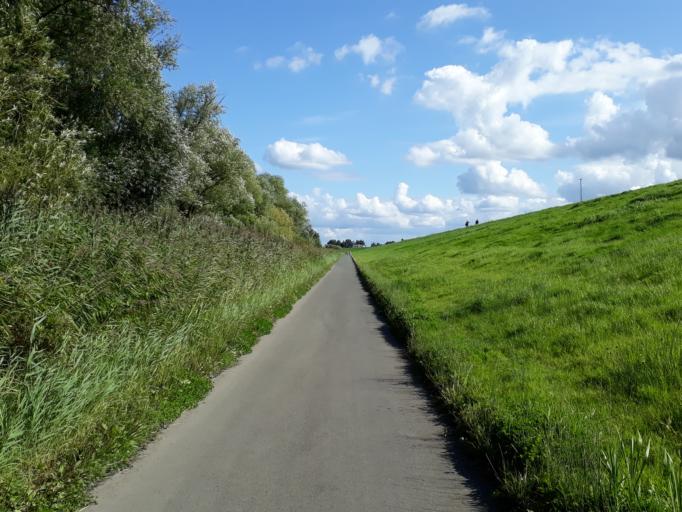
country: DE
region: Lower Saxony
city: Jork
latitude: 53.5587
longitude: 9.6604
